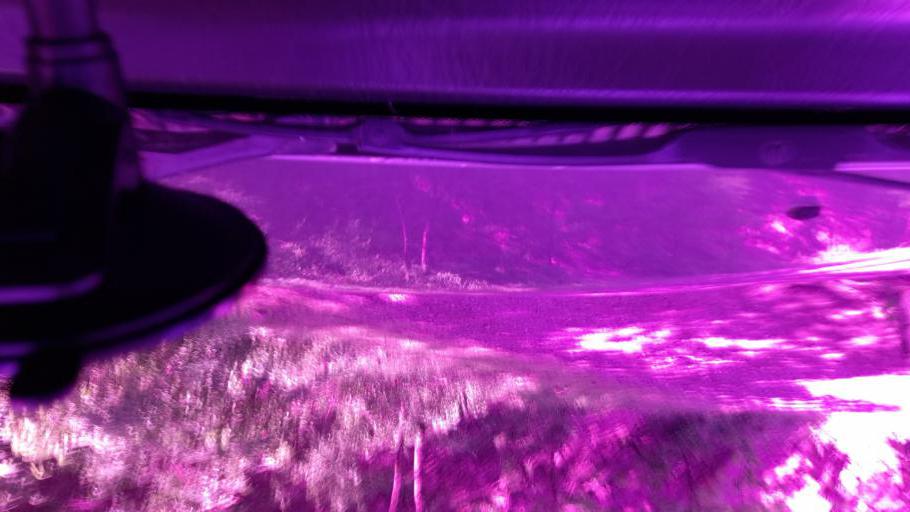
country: ET
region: Oromiya
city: Jima
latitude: 7.8037
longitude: 37.5272
